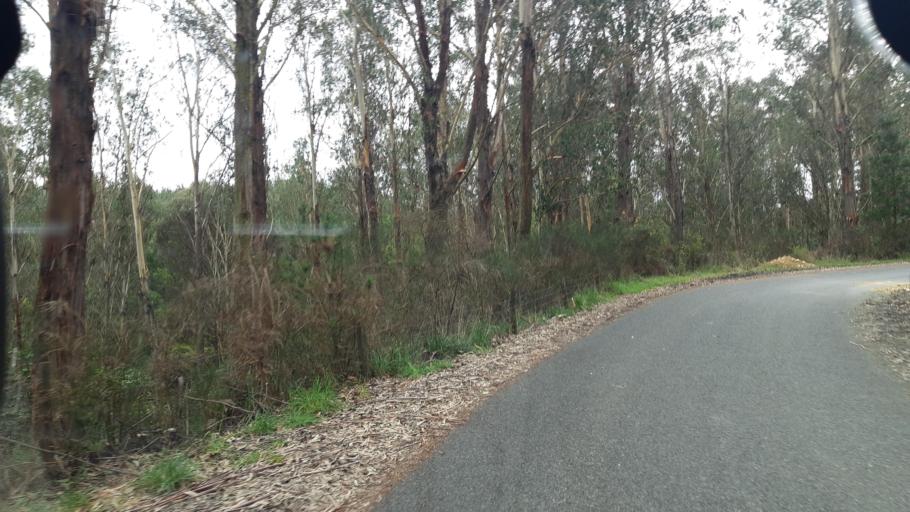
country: NZ
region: Tasman
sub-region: Tasman District
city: Motueka
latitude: -41.2656
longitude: 172.8873
